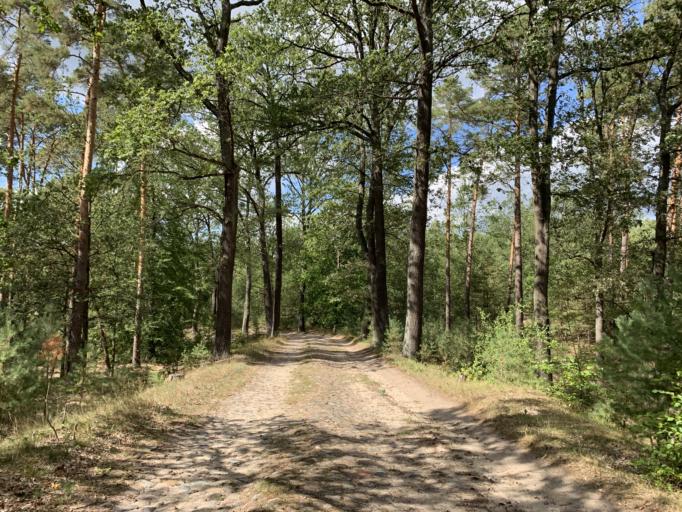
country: DE
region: Brandenburg
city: Michendorf
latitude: 52.3205
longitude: 12.9974
